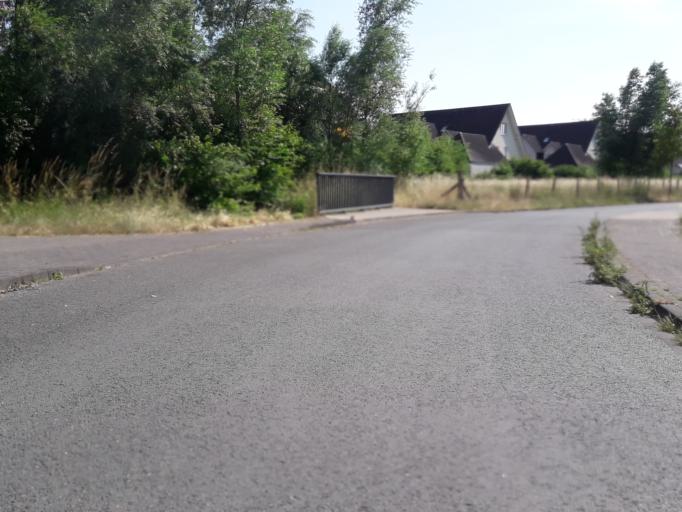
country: DE
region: North Rhine-Westphalia
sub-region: Regierungsbezirk Detmold
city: Paderborn
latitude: 51.7331
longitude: 8.7593
